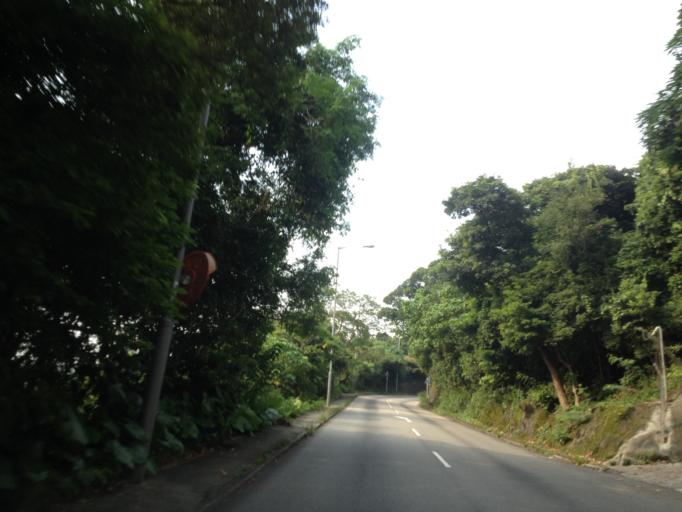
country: HK
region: Wanchai
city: Wan Chai
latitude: 22.2635
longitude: 114.2302
